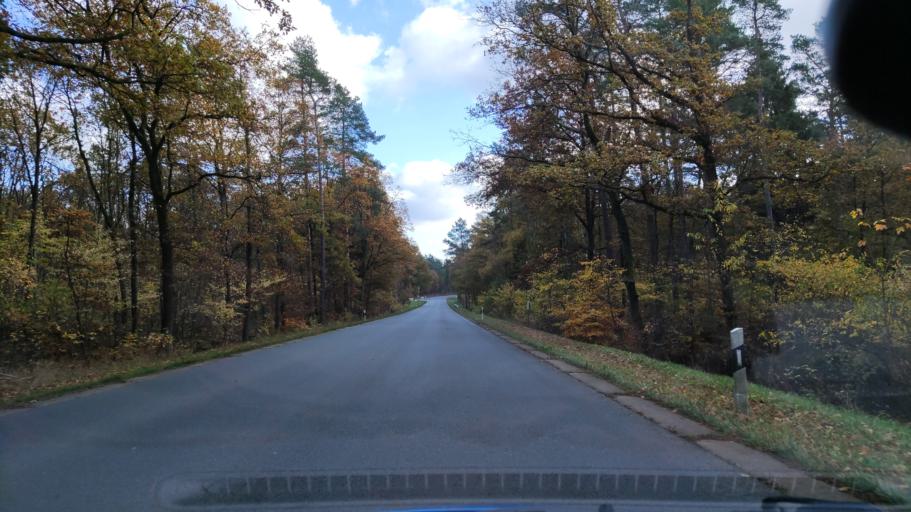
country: DE
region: Lower Saxony
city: Munster
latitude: 53.0138
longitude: 10.0948
